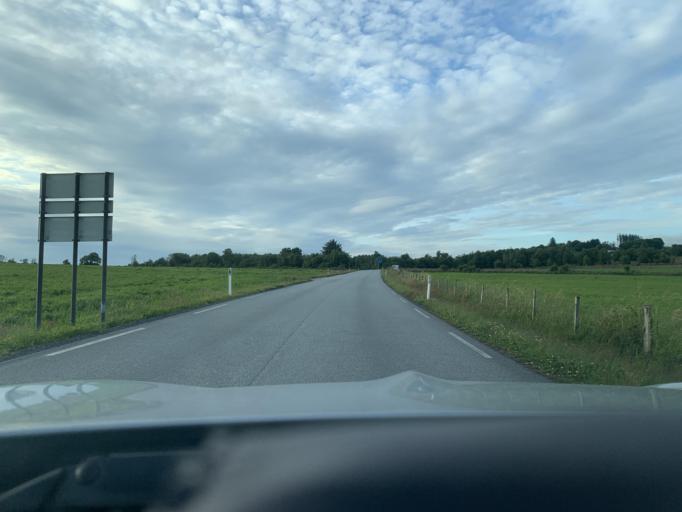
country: NO
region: Rogaland
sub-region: Time
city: Bryne
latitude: 58.6956
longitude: 5.7101
